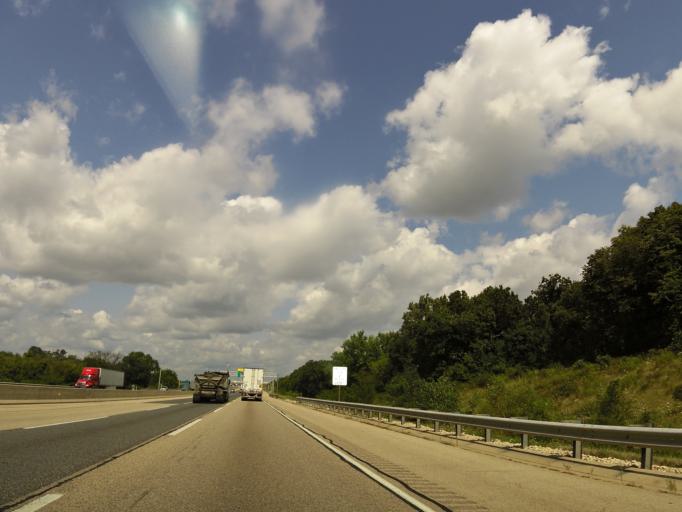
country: US
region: Illinois
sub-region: Winnebago County
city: Roscoe
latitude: 42.4332
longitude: -88.9882
